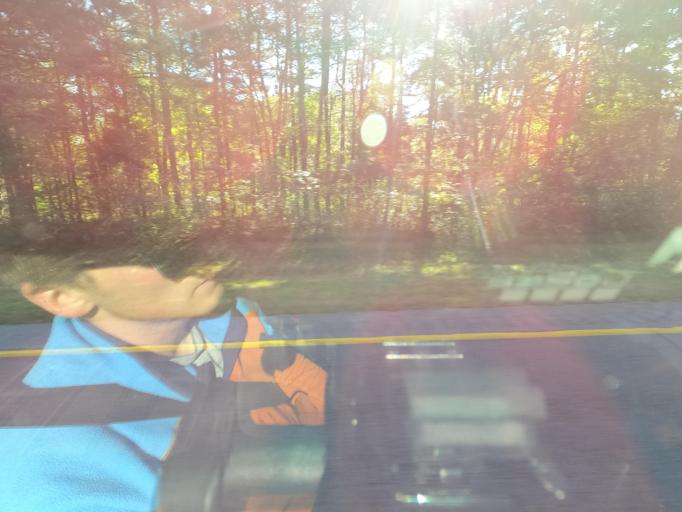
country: US
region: Tennessee
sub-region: Cheatham County
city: Kingston Springs
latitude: 36.0575
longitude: -87.1376
